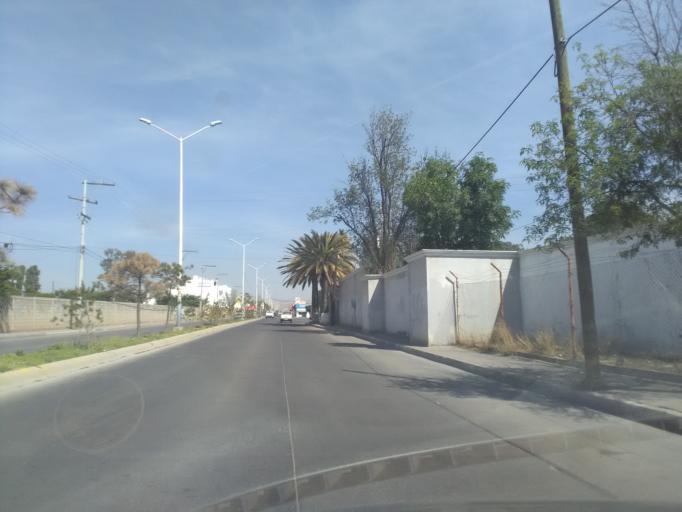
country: MX
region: Durango
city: Victoria de Durango
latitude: 24.0522
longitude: -104.6267
